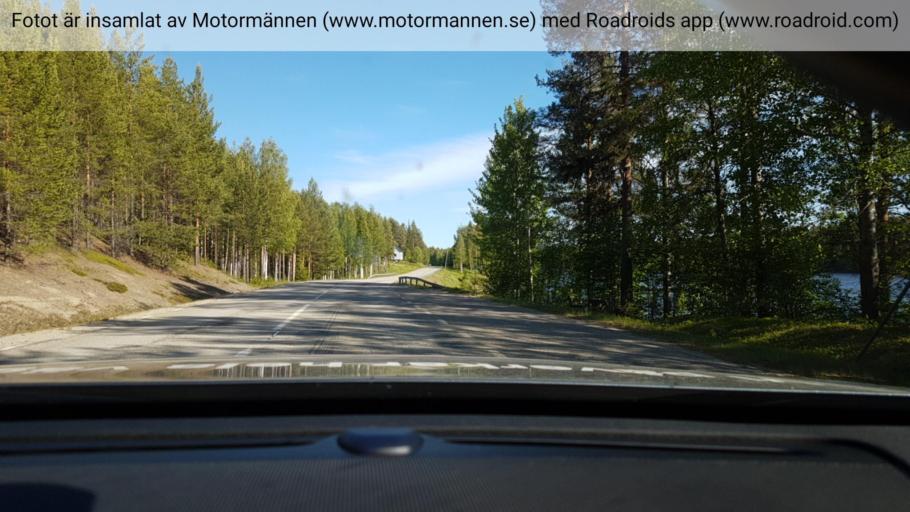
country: SE
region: Vaesterbotten
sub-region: Lycksele Kommun
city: Lycksele
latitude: 64.7783
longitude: 19.0090
